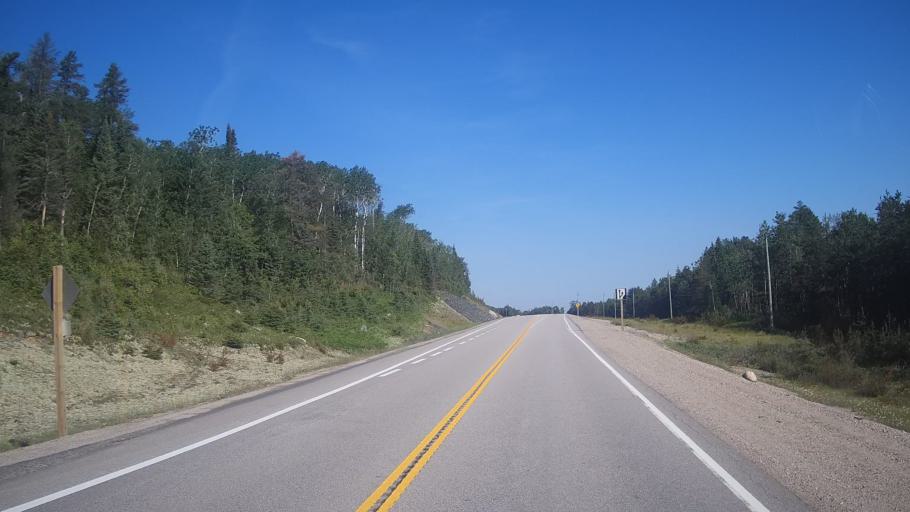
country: CA
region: Ontario
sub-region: Rainy River District
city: Atikokan
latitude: 49.4804
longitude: -91.9527
